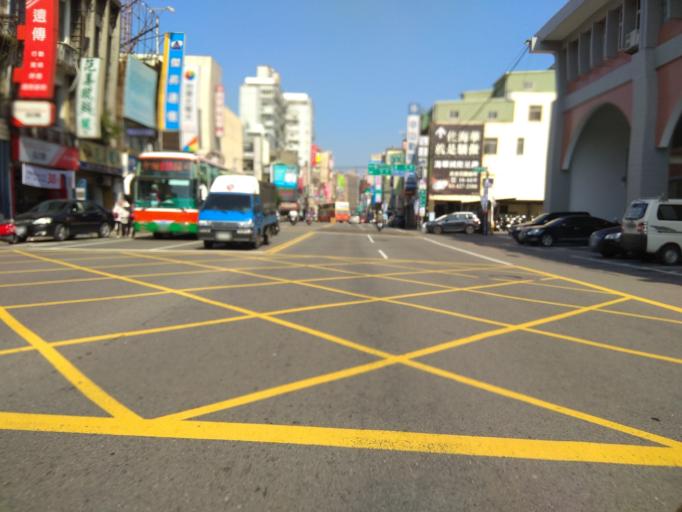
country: TW
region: Taiwan
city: Taoyuan City
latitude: 24.9541
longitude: 121.2222
